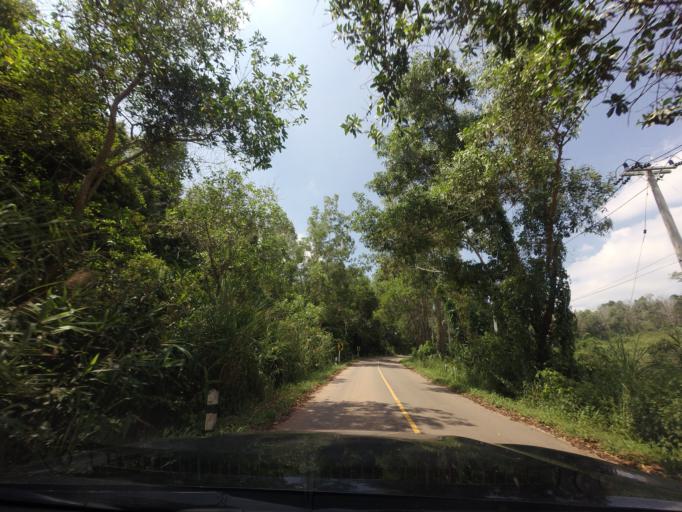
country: TH
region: Loei
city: Na Haeo
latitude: 17.4927
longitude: 100.8888
